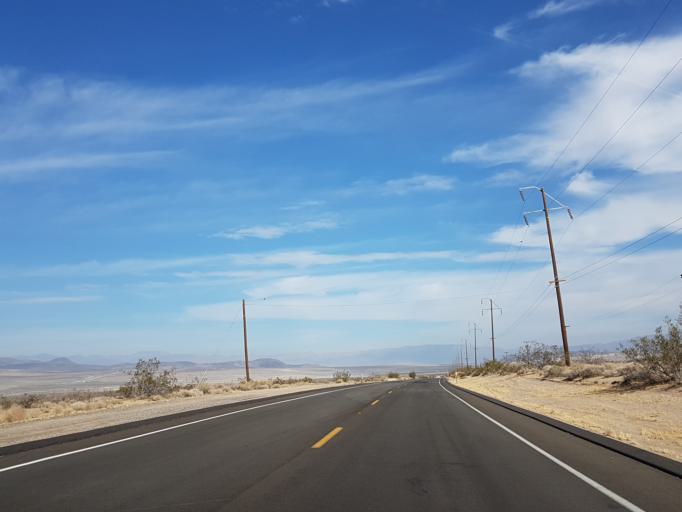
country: US
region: California
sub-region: Kern County
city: Ridgecrest
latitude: 35.6390
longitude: -117.5633
